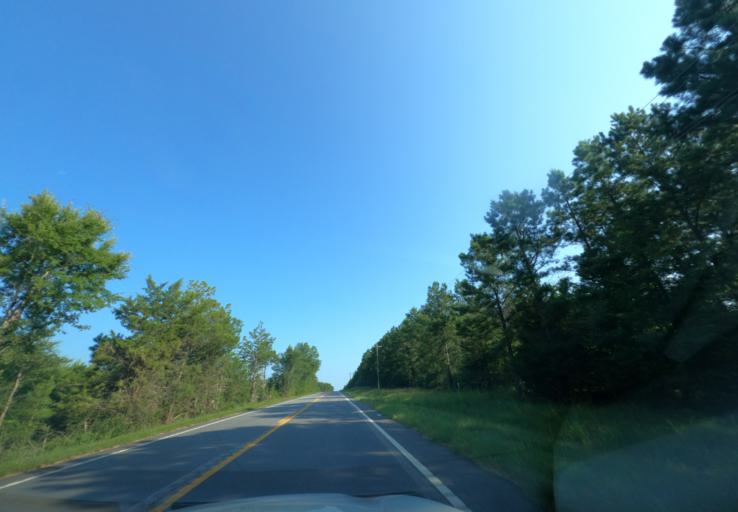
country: US
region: South Carolina
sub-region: Edgefield County
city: Edgefield
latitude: 33.8407
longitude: -81.9741
